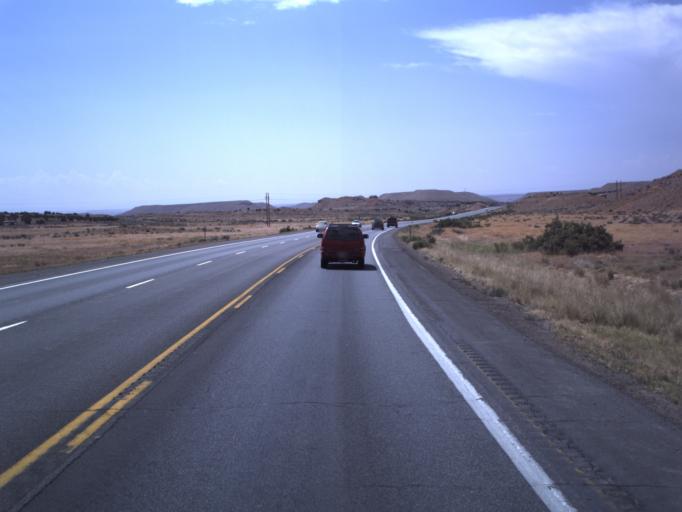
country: US
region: Utah
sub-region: Uintah County
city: Maeser
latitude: 40.3954
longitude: -109.5929
